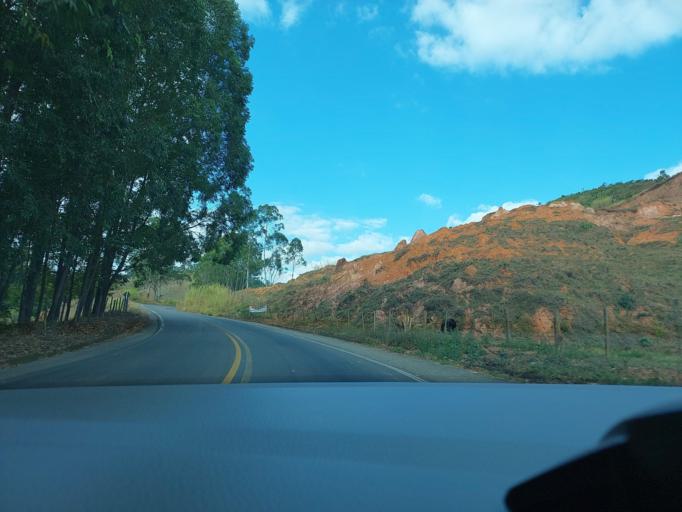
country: BR
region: Minas Gerais
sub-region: Vicosa
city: Vicosa
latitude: -20.8391
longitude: -42.7186
